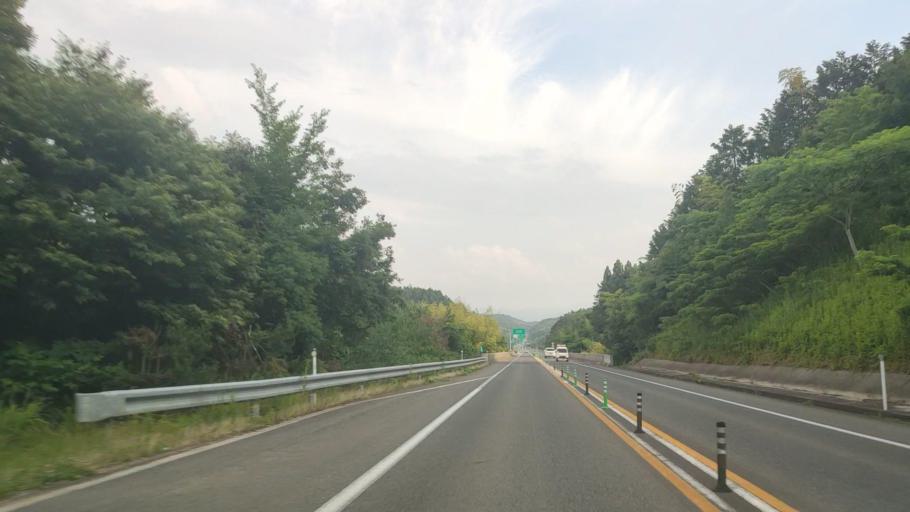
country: JP
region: Tottori
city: Kurayoshi
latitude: 35.4713
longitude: 133.8073
